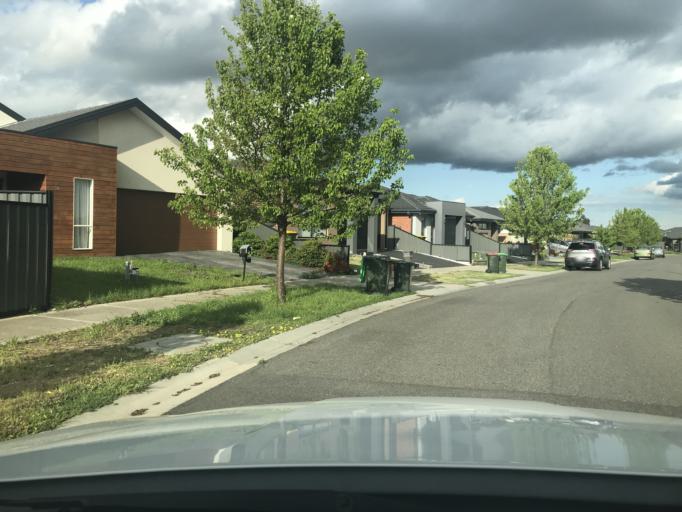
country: AU
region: Victoria
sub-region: Hume
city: Craigieburn
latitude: -37.5780
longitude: 144.9032
